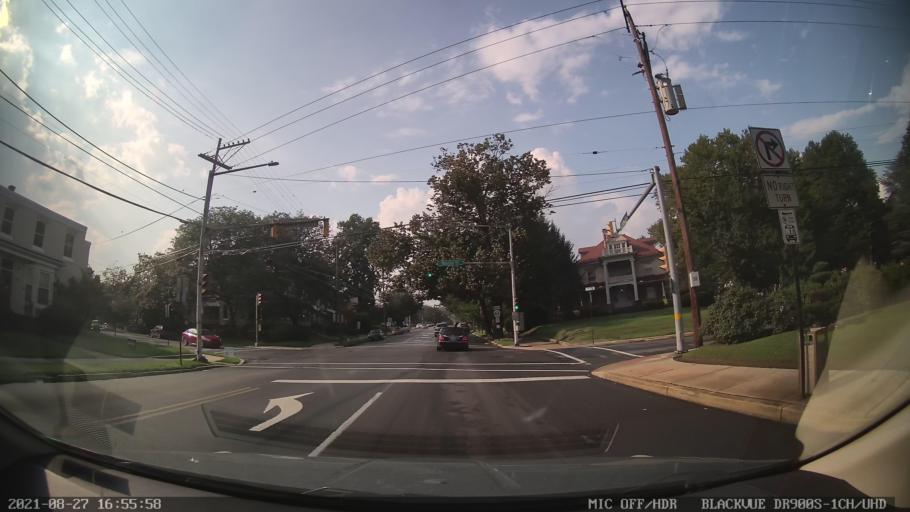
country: US
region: Pennsylvania
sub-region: Berks County
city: Reading
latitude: 40.3488
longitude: -75.9316
